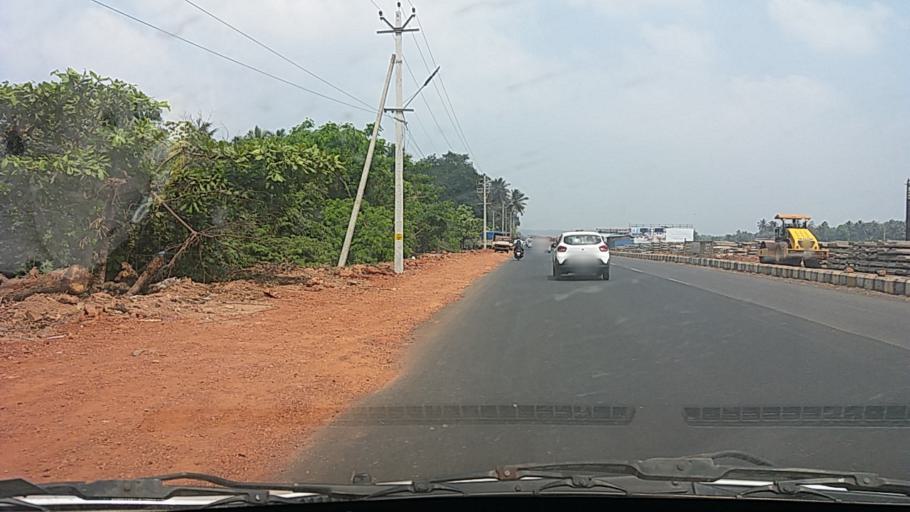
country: IN
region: Goa
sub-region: North Goa
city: Bambolim
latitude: 15.4740
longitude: 73.8499
